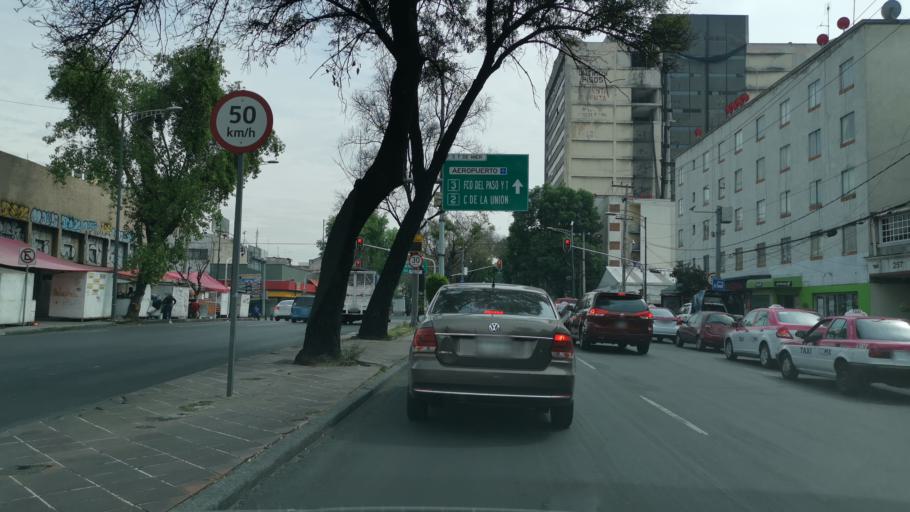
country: MX
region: Mexico City
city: Mexico City
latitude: 19.4237
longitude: -99.1316
